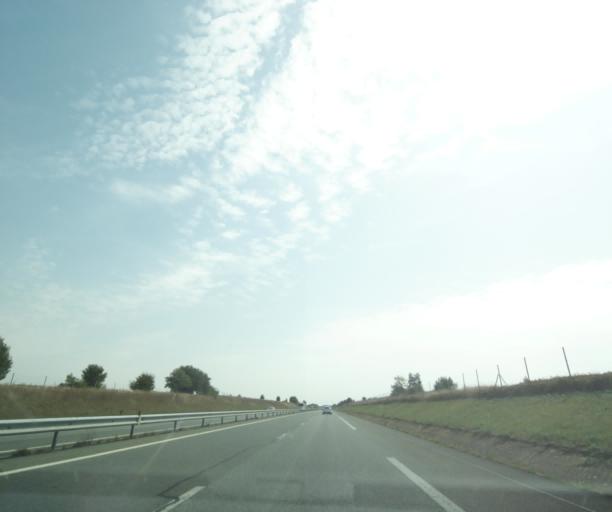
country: FR
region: Pays de la Loire
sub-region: Departement de la Vendee
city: Le Langon
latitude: 46.4831
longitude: -0.9505
